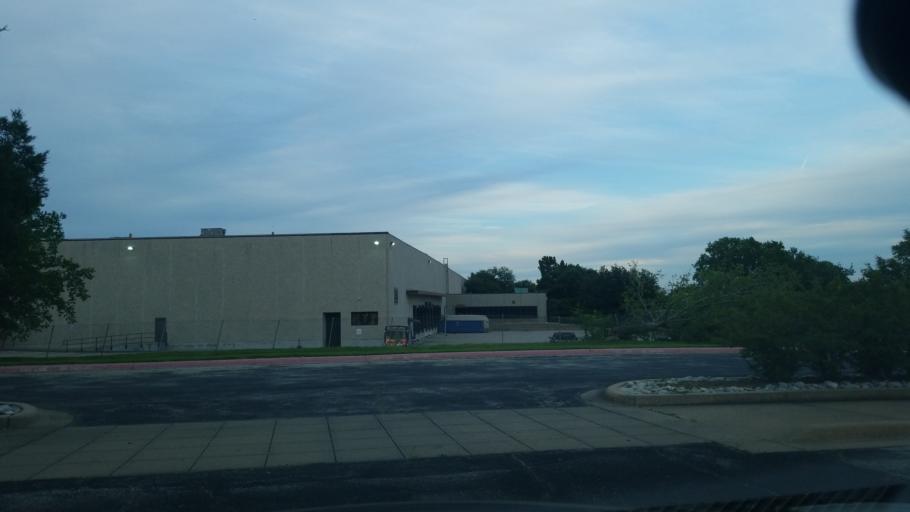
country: US
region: Texas
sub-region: Dallas County
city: Irving
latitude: 32.8730
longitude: -96.9777
